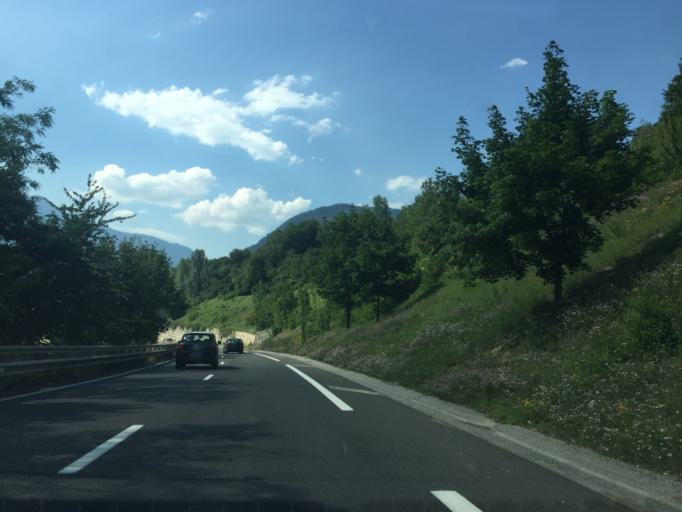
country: FR
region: Rhone-Alpes
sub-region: Departement de la Savoie
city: Aigueblanche
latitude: 45.5105
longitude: 6.5017
